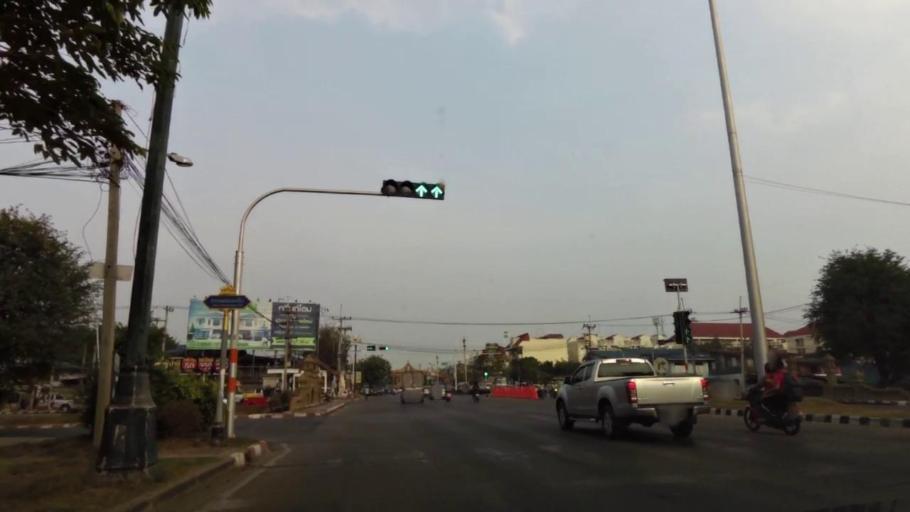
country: TH
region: Phra Nakhon Si Ayutthaya
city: Phra Nakhon Si Ayutthaya
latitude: 14.3513
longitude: 100.5752
